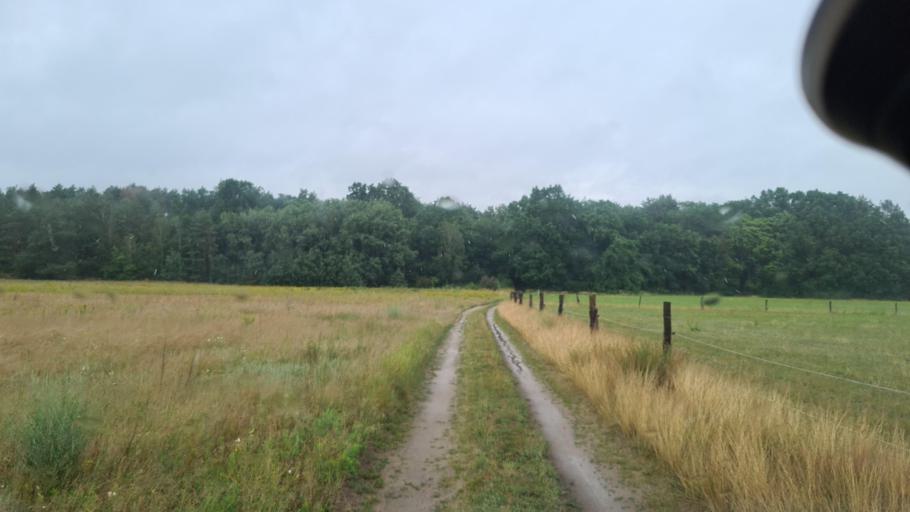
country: DE
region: Brandenburg
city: Juterbog
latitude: 51.9884
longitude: 13.1685
